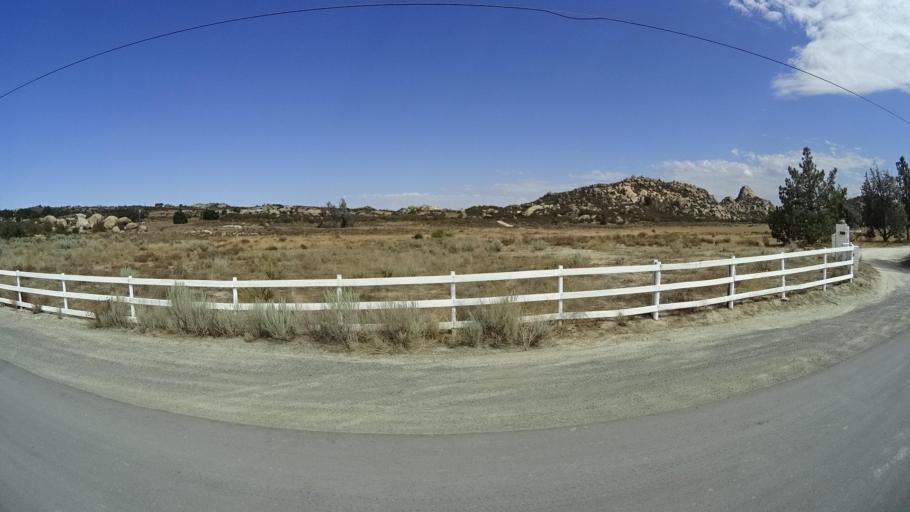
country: MX
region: Baja California
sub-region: Tecate
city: Cereso del Hongo
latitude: 32.6396
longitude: -116.2729
